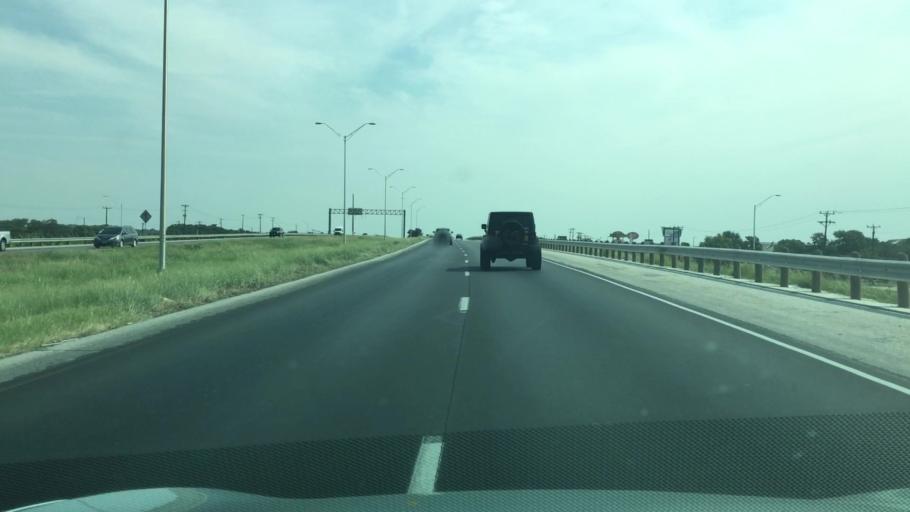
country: US
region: Texas
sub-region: Bexar County
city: Helotes
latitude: 29.5663
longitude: -98.6538
